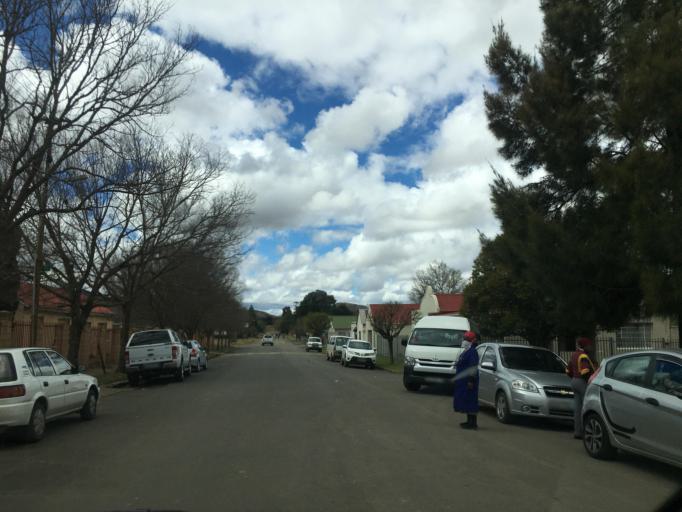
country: ZA
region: Eastern Cape
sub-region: Chris Hani District Municipality
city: Elliot
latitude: -31.3303
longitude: 27.8512
